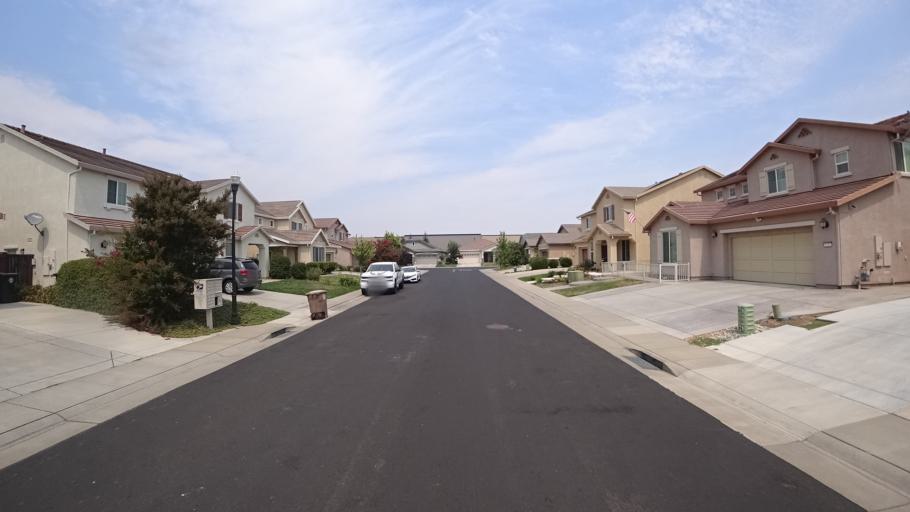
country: US
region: California
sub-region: Sacramento County
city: Laguna
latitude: 38.4043
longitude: -121.4142
